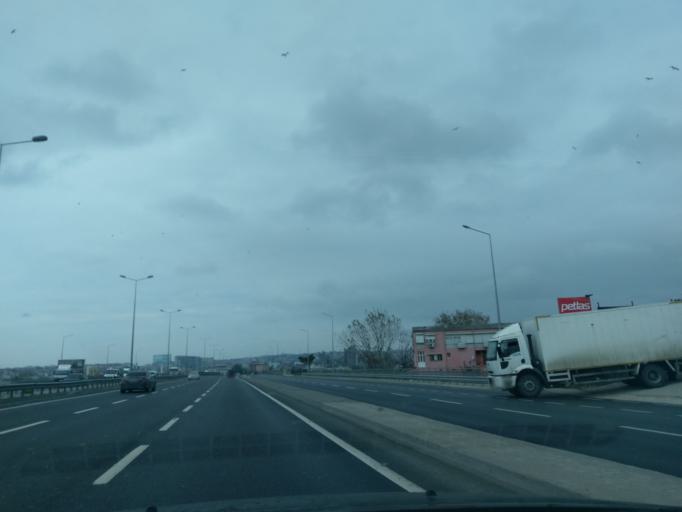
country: TR
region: Istanbul
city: Bueyuekcekmece
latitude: 41.0197
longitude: 28.5751
